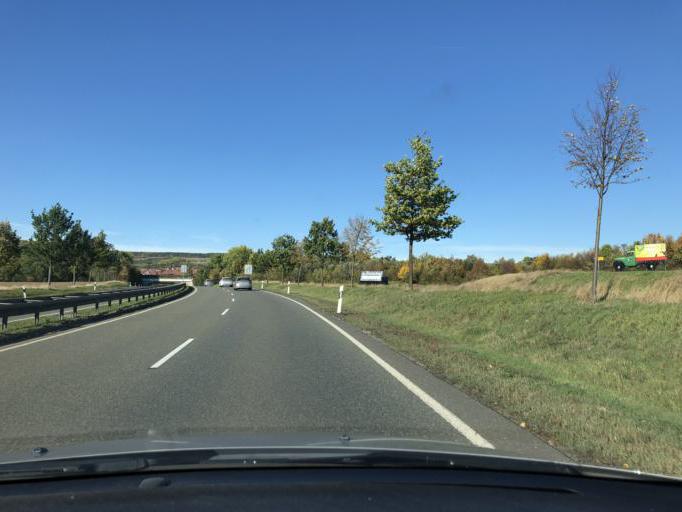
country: DE
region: Thuringia
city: Hopfgarten
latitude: 50.9868
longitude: 11.2920
